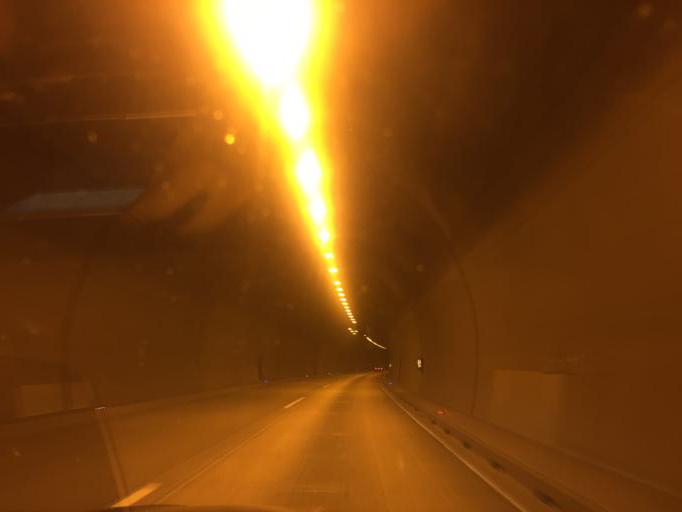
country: SI
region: Zagorje ob Savi
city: Izlake
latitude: 46.1894
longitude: 14.8949
